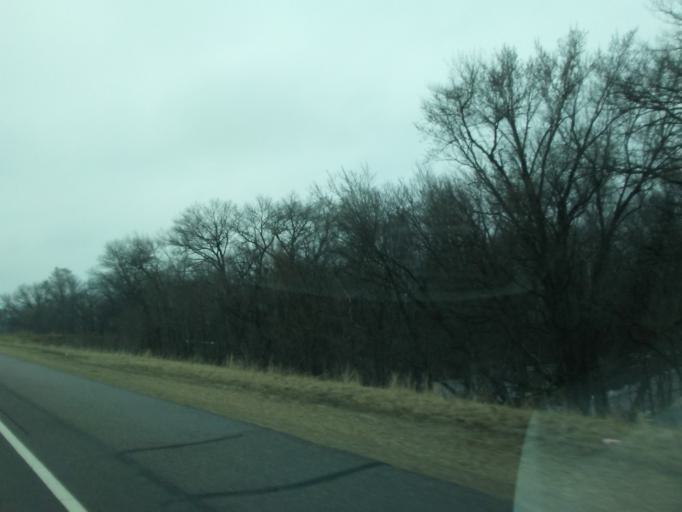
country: US
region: Wisconsin
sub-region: Sauk County
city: Spring Green
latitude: 43.1732
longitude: -90.0474
